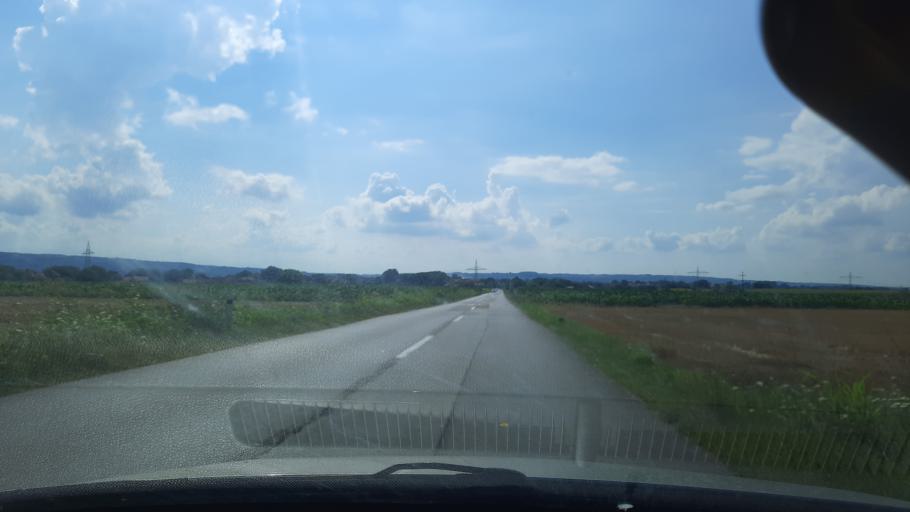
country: RS
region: Central Serbia
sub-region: Branicevski Okrug
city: Malo Crnice
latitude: 44.5860
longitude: 21.2868
